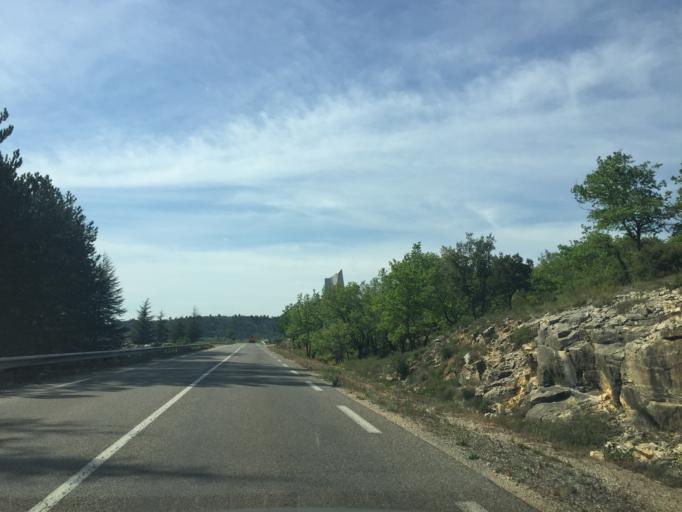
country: FR
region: Provence-Alpes-Cote d'Azur
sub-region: Departement du Var
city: Ginasservis
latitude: 43.6955
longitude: 5.8343
